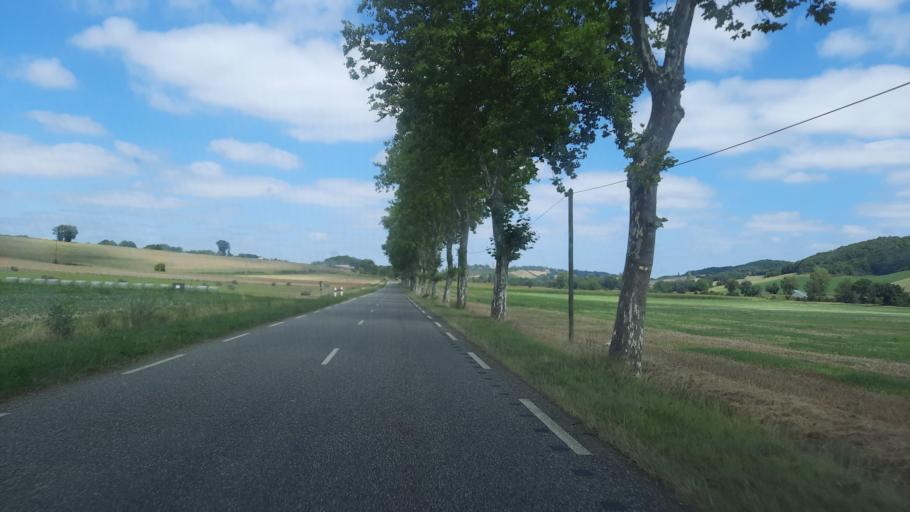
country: FR
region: Midi-Pyrenees
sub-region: Departement de la Haute-Garonne
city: Boulogne-sur-Gesse
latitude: 43.3583
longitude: 0.7300
